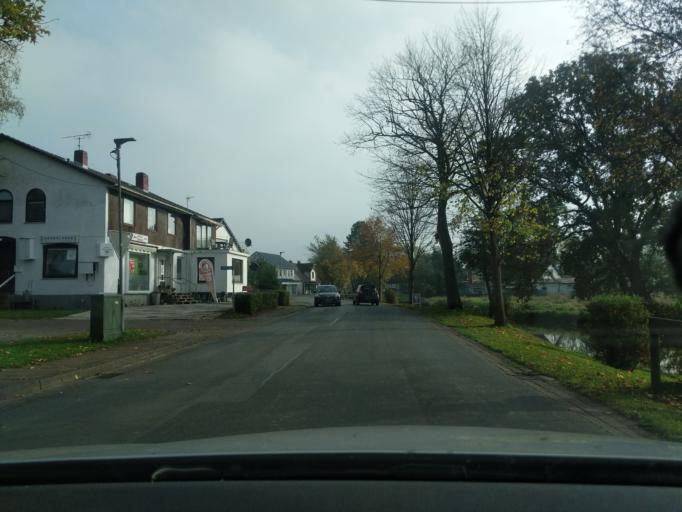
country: DE
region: Lower Saxony
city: Ihlienworth
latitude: 53.7379
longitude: 8.9192
